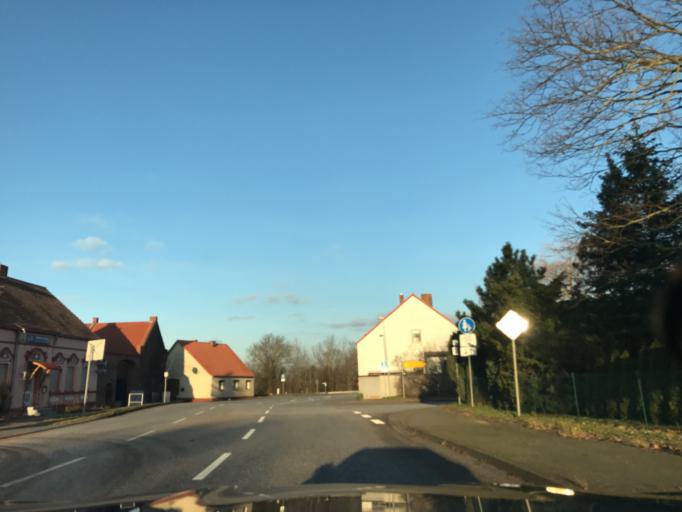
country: DE
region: Saxony-Anhalt
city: Burg bei Magdeburg
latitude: 52.3137
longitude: 12.0060
